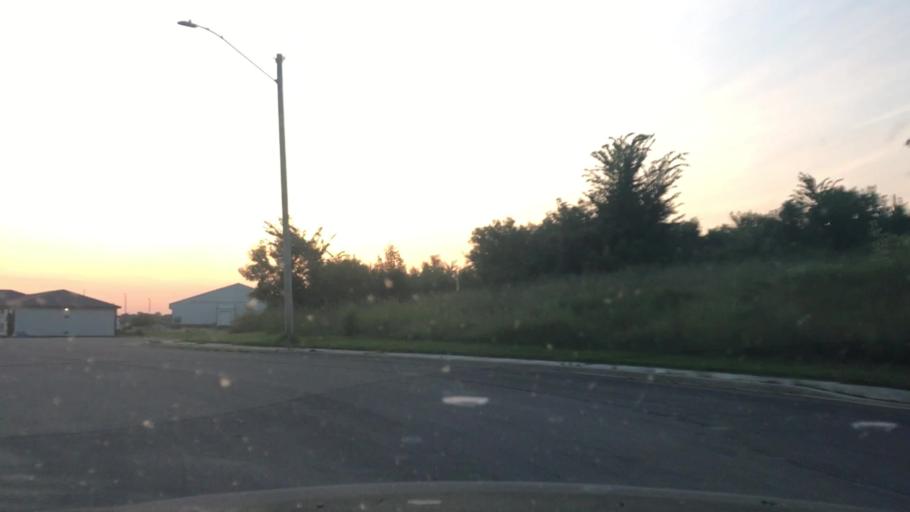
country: US
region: Minnesota
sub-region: Redwood County
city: Redwood Falls
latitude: 44.5496
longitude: -94.9902
